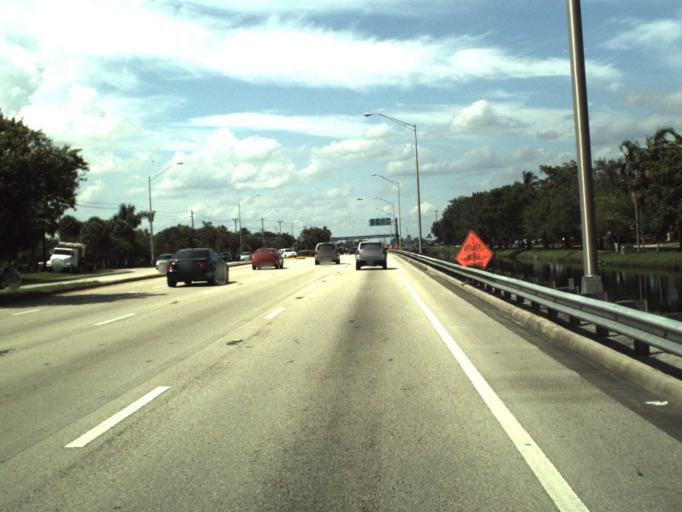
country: US
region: Florida
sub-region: Broward County
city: Miramar
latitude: 25.9904
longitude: -80.2474
